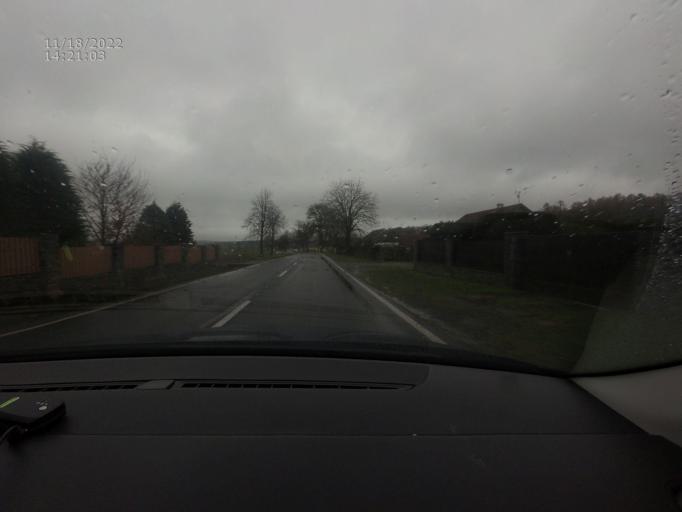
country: CZ
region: Jihocesky
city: Cimelice
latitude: 49.4420
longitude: 14.0847
